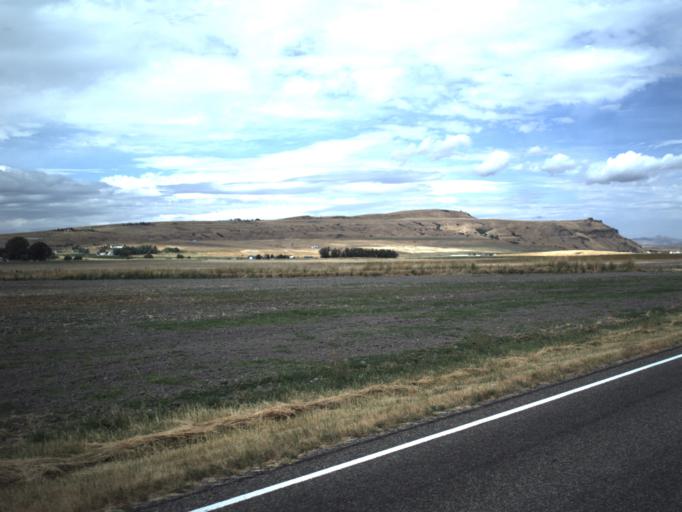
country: US
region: Utah
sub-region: Cache County
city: Mendon
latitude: 41.7564
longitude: -111.9794
